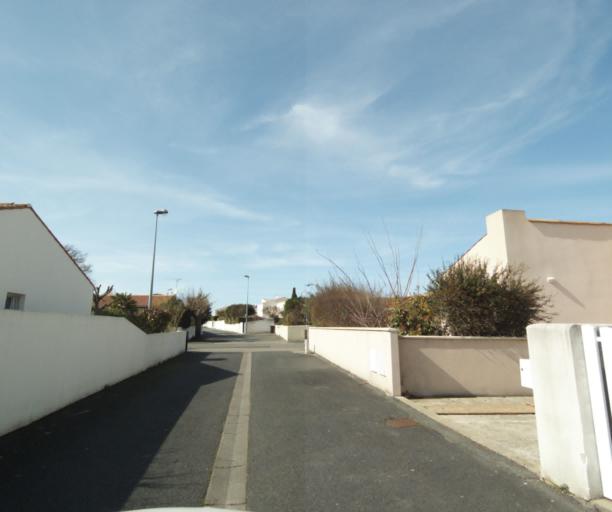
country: FR
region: Poitou-Charentes
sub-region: Departement de la Charente-Maritime
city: Lagord
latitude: 46.1835
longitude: -1.1642
